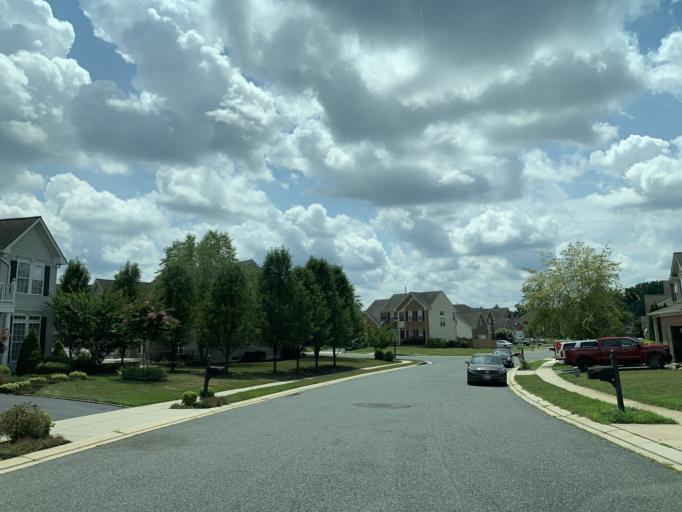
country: US
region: Maryland
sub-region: Harford County
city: Bel Air North
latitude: 39.5577
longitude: -76.3589
